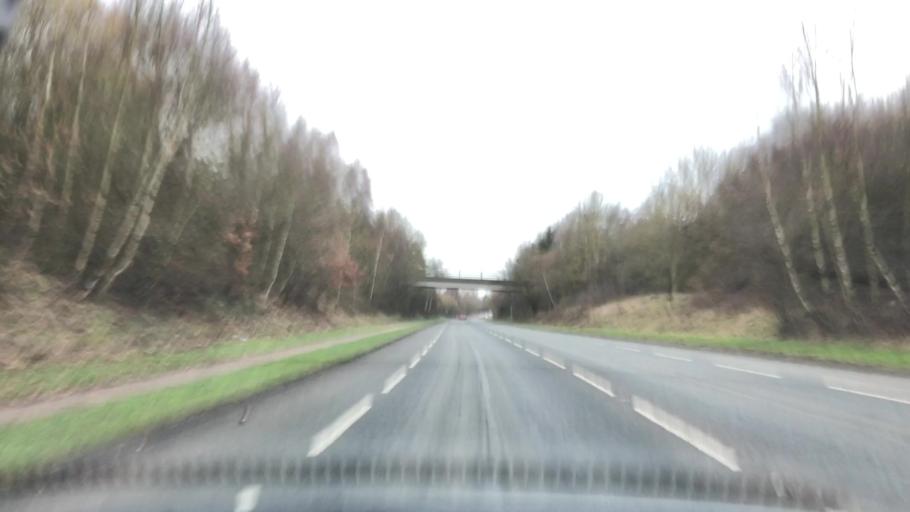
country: GB
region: England
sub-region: Coventry
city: Keresley
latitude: 52.4276
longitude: -1.5508
